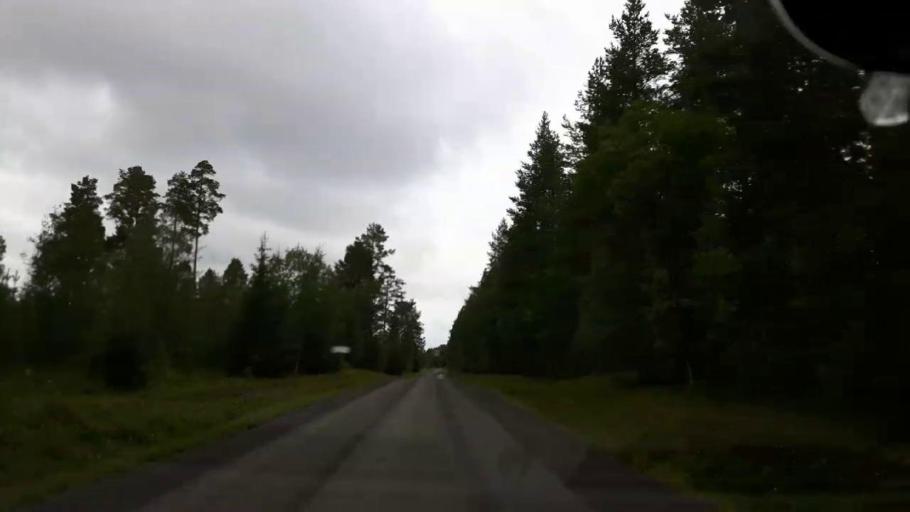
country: SE
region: Jaemtland
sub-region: OEstersunds Kommun
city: Ostersund
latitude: 63.0422
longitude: 14.5760
